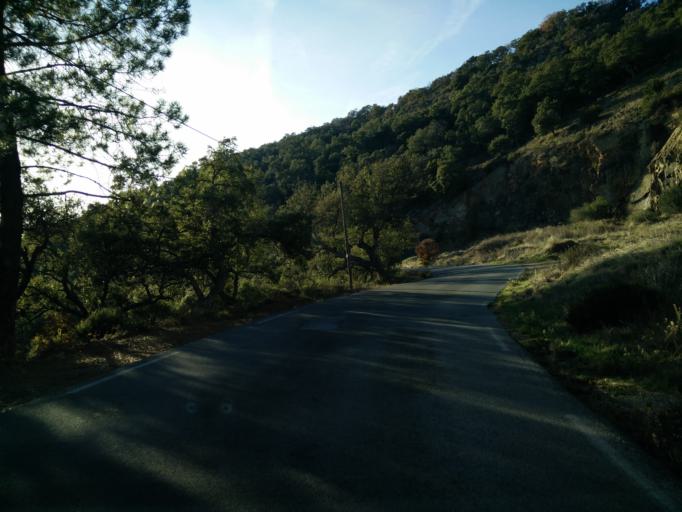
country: FR
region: Provence-Alpes-Cote d'Azur
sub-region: Departement du Var
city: La Garde-Freinet
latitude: 43.3367
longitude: 6.5027
